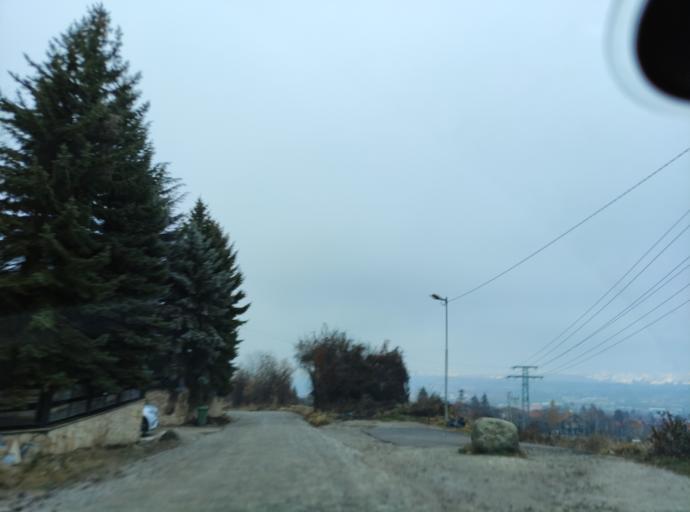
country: BG
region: Sofia-Capital
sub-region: Stolichna Obshtina
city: Sofia
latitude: 42.6228
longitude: 23.3092
